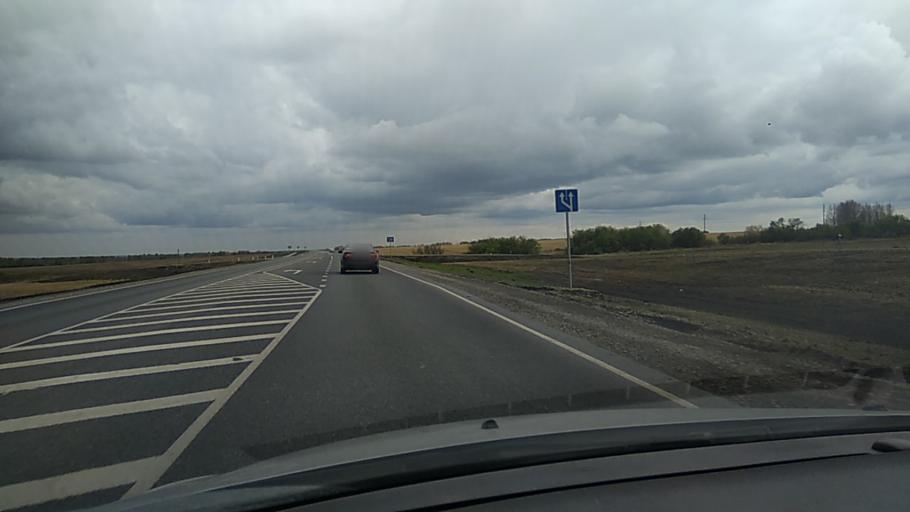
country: RU
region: Kurgan
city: Dalmatovo
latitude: 56.2895
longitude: 62.7844
